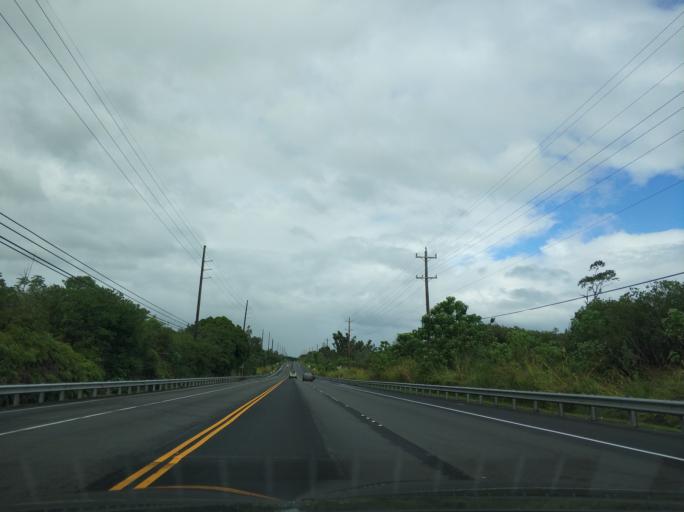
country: US
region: Hawaii
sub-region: Hawaii County
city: Kea'au
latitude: 19.5949
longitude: -155.0182
